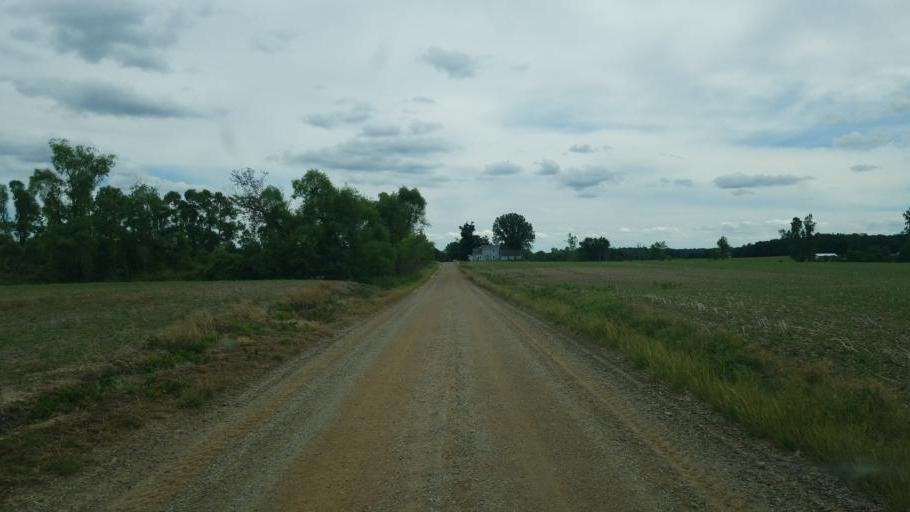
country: US
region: Michigan
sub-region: Barry County
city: Nashville
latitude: 42.6585
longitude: -84.9755
